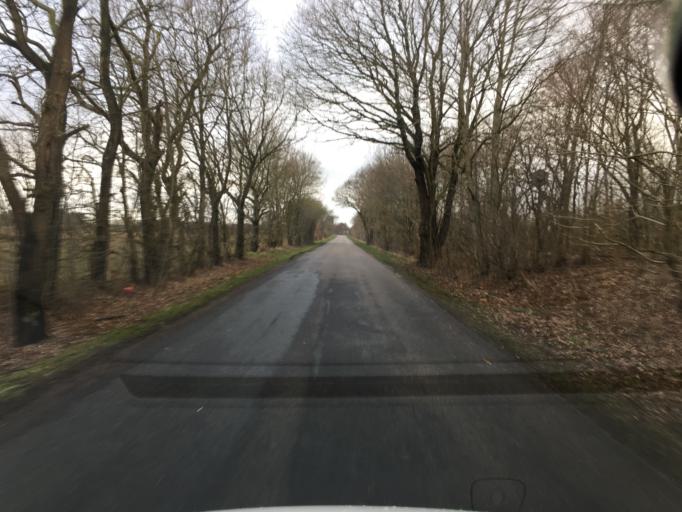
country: DE
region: Schleswig-Holstein
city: Bramstedtlund
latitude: 54.9426
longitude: 9.1041
